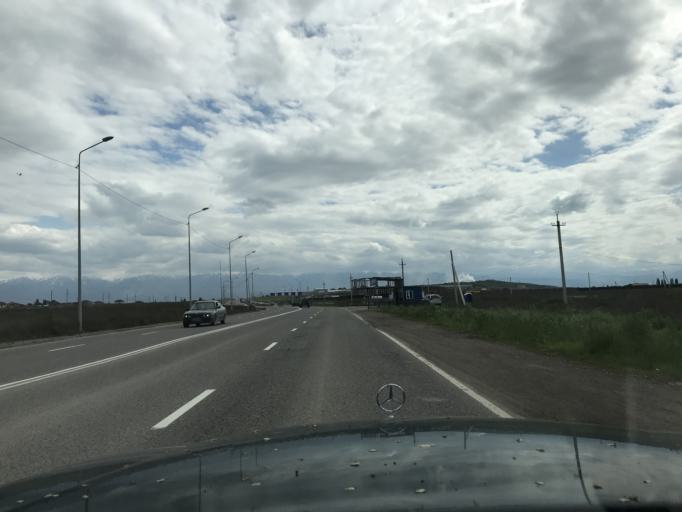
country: KZ
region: Almaty Oblysy
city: Burunday
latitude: 43.3500
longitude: 76.8340
